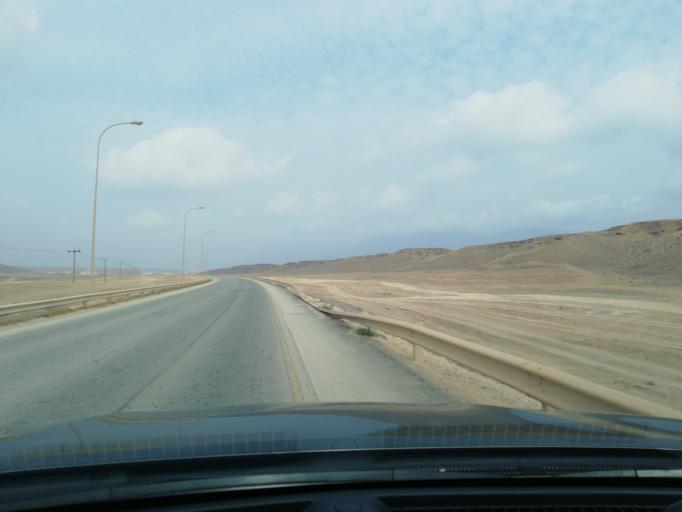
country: OM
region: Zufar
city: Salalah
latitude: 16.9606
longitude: 53.8905
